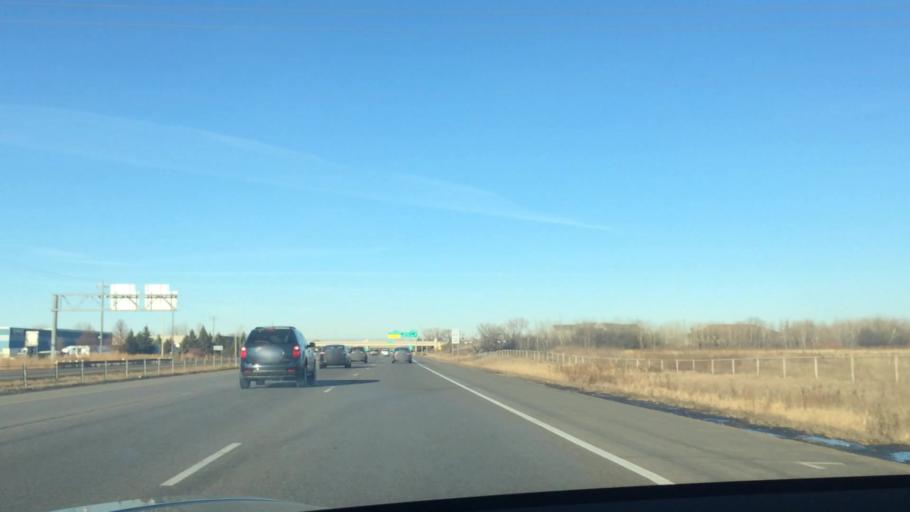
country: US
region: Minnesota
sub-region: Ramsey County
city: Mounds View
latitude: 45.1188
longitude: -93.1884
